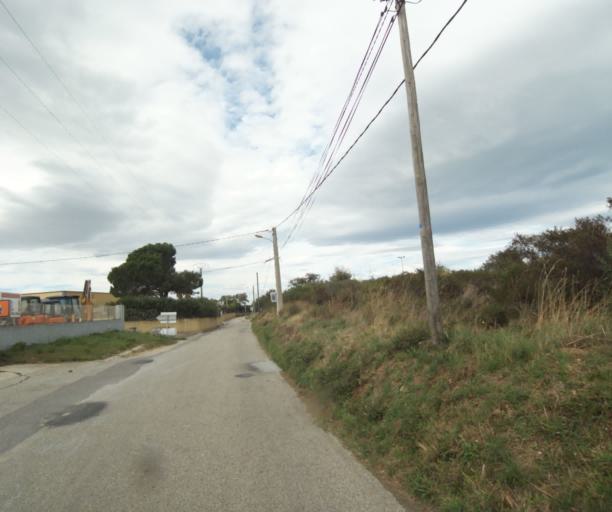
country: FR
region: Languedoc-Roussillon
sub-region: Departement des Pyrenees-Orientales
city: Sant Andreu de Sureda
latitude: 42.5485
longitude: 2.9910
